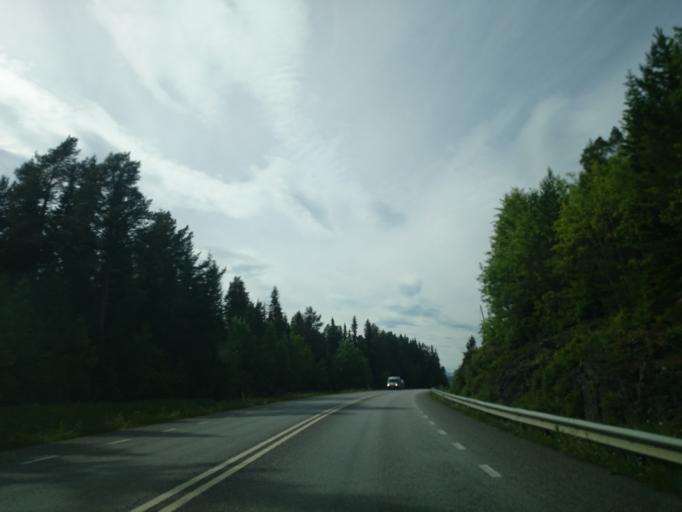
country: SE
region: Jaemtland
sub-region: Are Kommun
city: Jarpen
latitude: 63.3368
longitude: 13.5026
